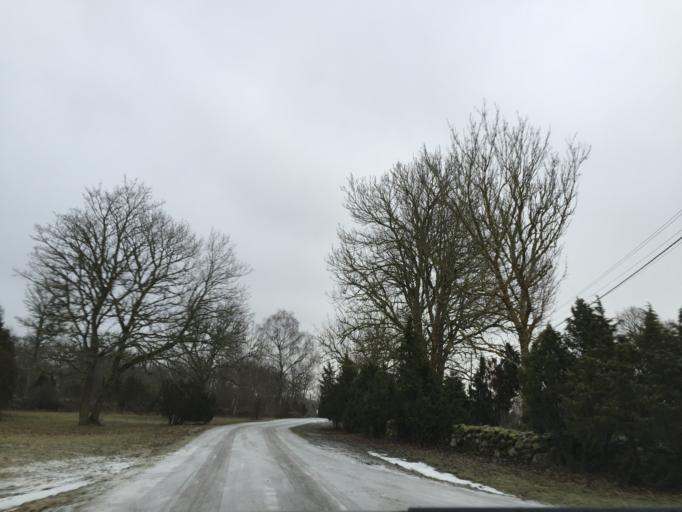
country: EE
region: Saare
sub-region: Orissaare vald
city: Orissaare
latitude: 58.5957
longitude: 23.0807
